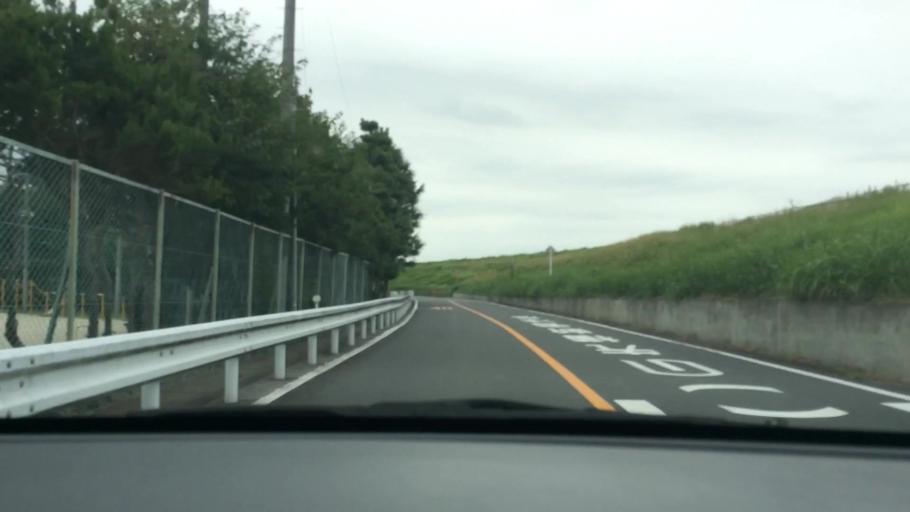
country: JP
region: Chiba
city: Matsudo
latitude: 35.8021
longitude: 139.8888
